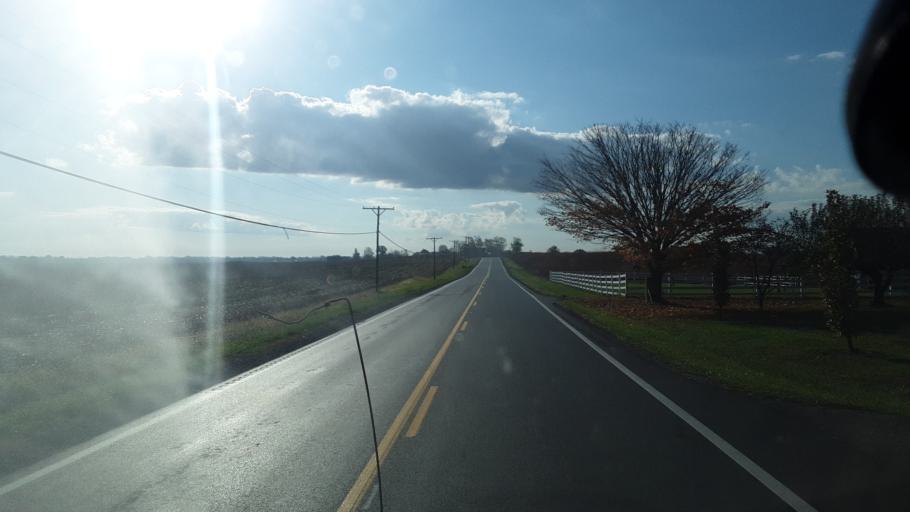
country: US
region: Ohio
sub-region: Fayette County
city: Jeffersonville
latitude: 39.6033
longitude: -83.5219
